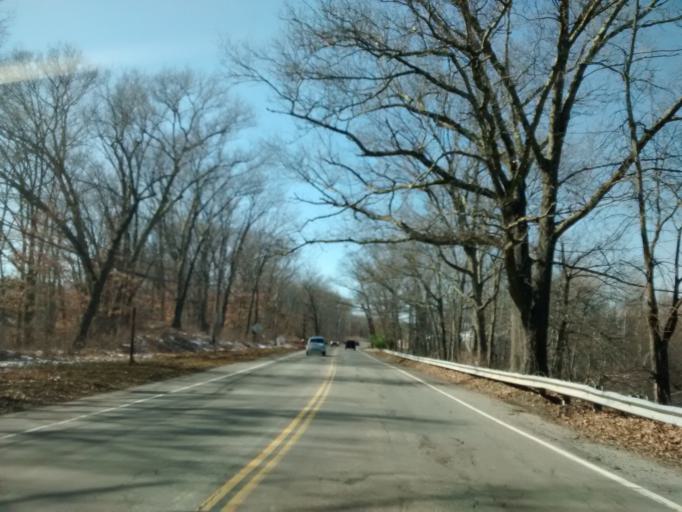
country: US
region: Massachusetts
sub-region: Worcester County
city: Millbury
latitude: 42.1815
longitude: -71.7341
